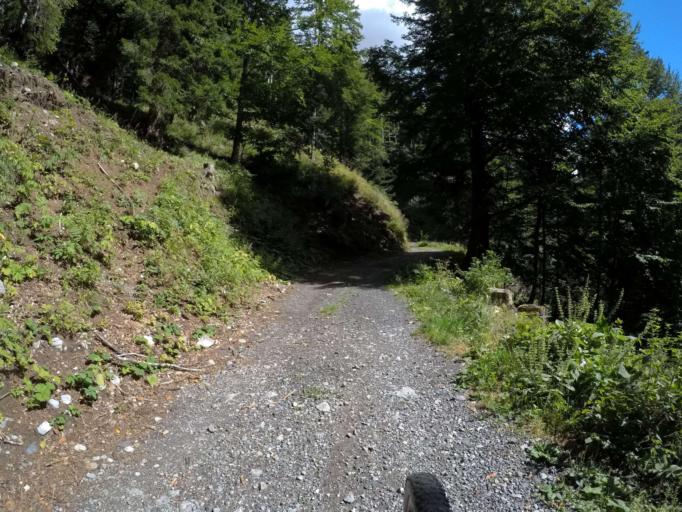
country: IT
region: Friuli Venezia Giulia
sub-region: Provincia di Udine
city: Paularo
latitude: 46.5641
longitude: 13.1277
